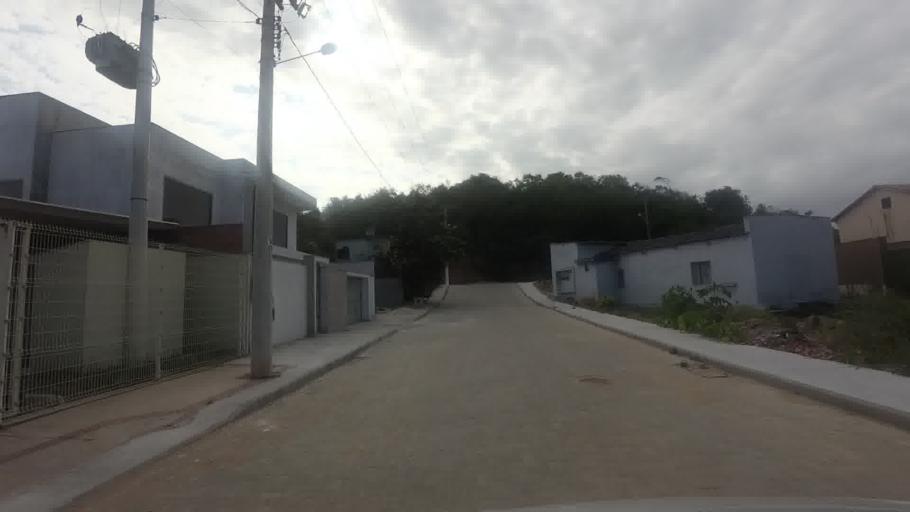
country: BR
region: Espirito Santo
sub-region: Itapemirim
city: Itapemirim
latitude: -21.0081
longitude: -40.8303
